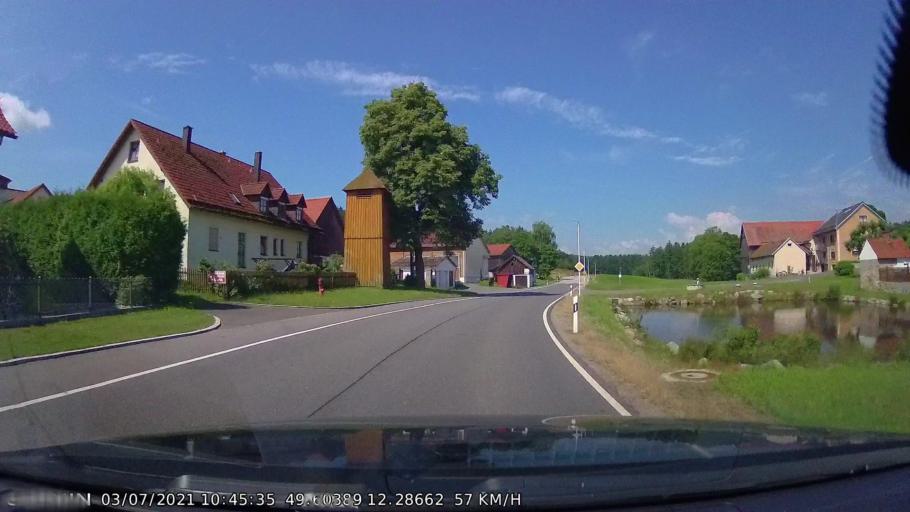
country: DE
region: Bavaria
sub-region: Upper Palatinate
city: Leuchtenberg
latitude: 49.6039
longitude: 12.2865
